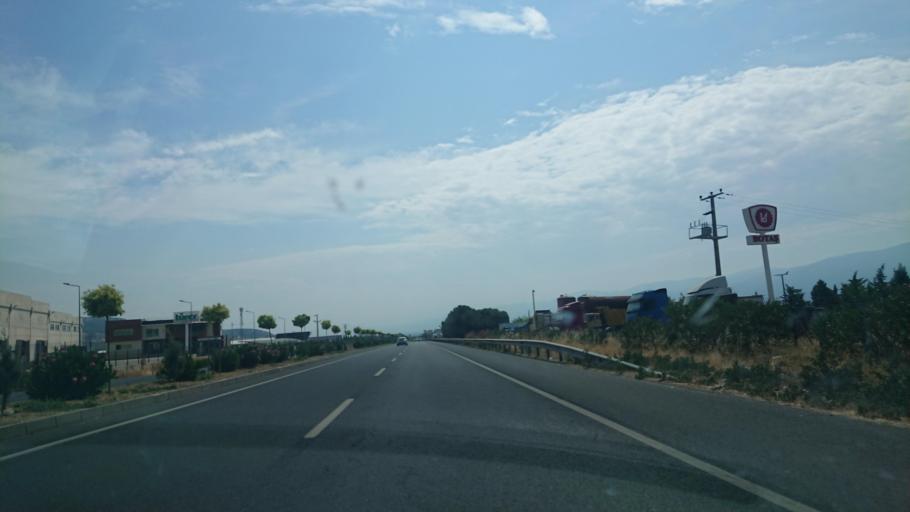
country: TR
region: Izmir
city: Kemalpasa
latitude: 38.4533
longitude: 27.4599
